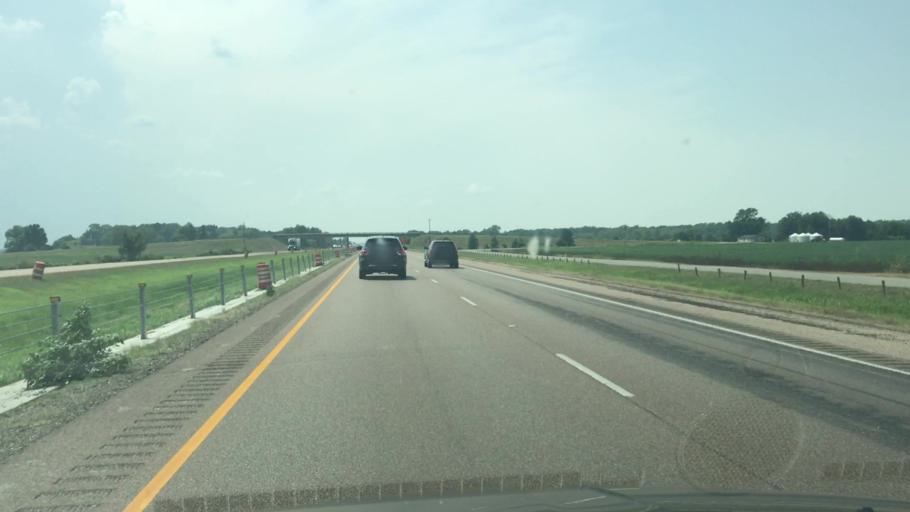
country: US
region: Arkansas
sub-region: Crittenden County
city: Earle
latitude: 35.1497
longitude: -90.3594
